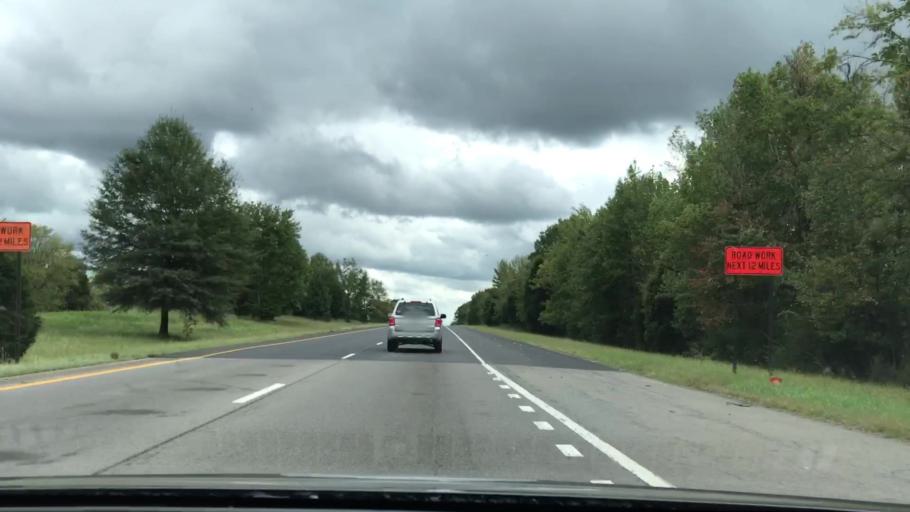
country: US
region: Tennessee
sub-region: Cheatham County
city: Pleasant View
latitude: 36.3977
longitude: -87.0177
